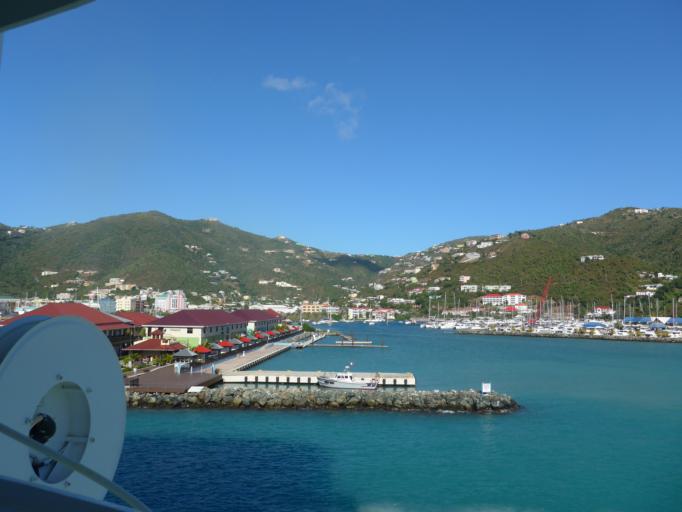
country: VG
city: Road Town
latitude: 18.4229
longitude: -64.6107
